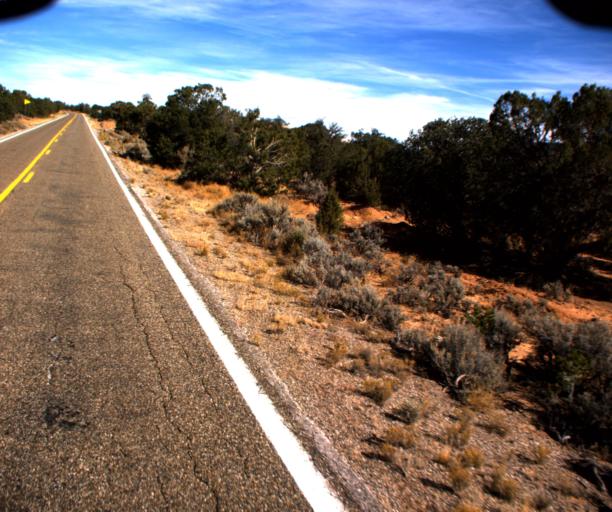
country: US
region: Arizona
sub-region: Navajo County
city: Kayenta
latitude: 36.5804
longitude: -110.4912
